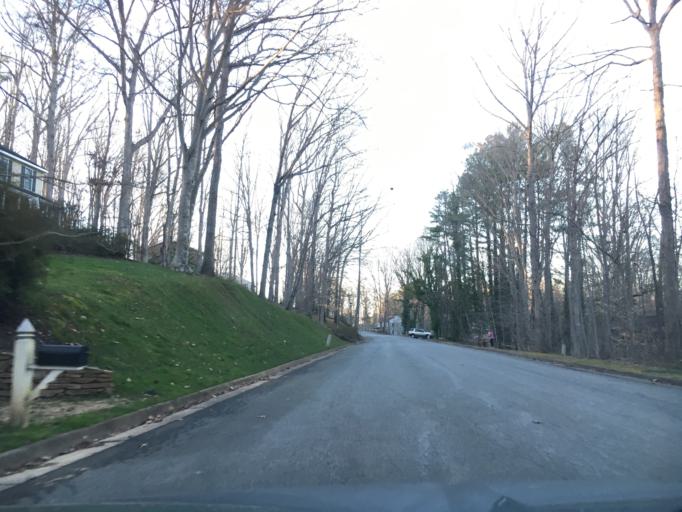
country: US
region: Virginia
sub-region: Halifax County
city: South Boston
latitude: 36.7181
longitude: -78.9138
